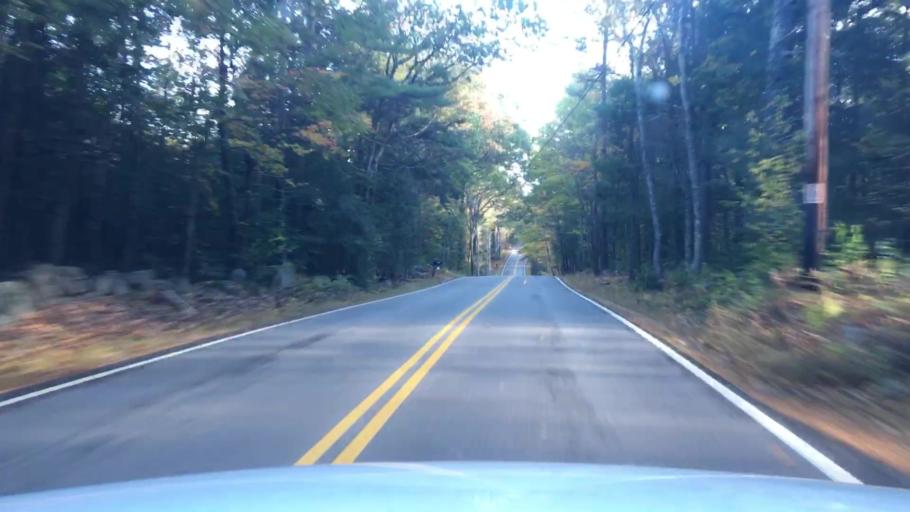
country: US
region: New Hampshire
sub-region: Strafford County
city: Barrington
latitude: 43.1690
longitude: -71.0507
